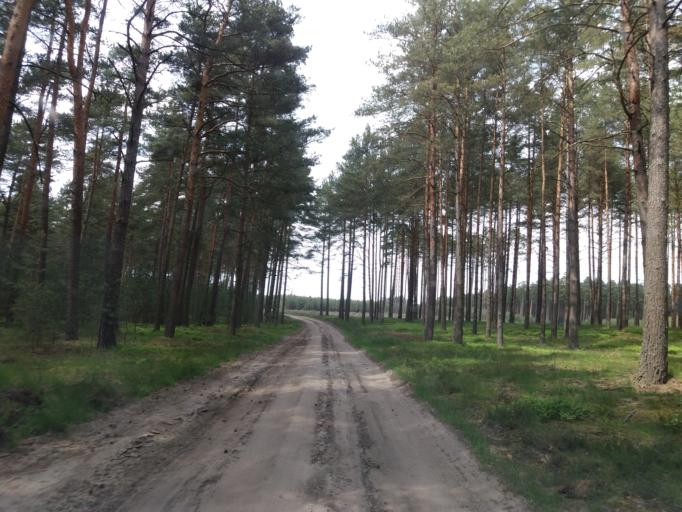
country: PL
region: West Pomeranian Voivodeship
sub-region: Powiat choszczenski
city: Drawno
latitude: 53.1593
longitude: 15.7564
